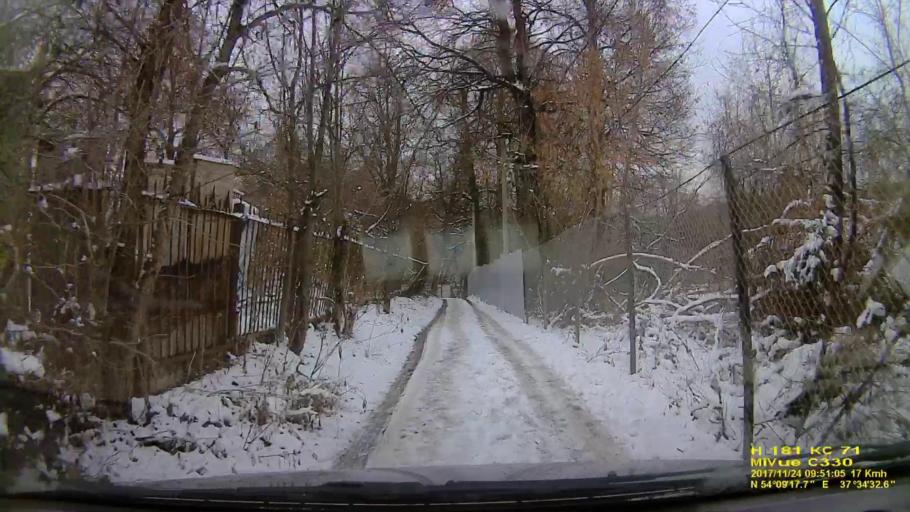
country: RU
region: Tula
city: Mendeleyevskiy
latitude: 54.1549
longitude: 37.5757
